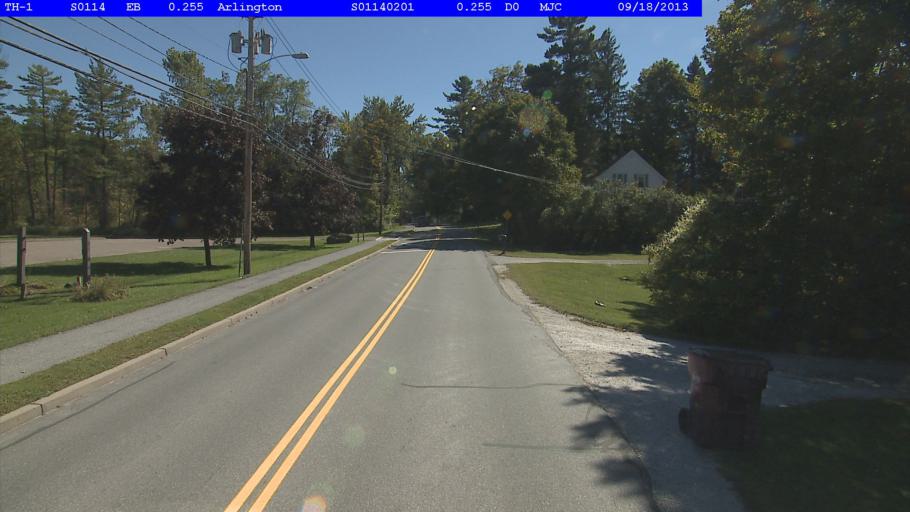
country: US
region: Vermont
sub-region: Bennington County
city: Arlington
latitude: 43.0694
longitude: -73.1537
